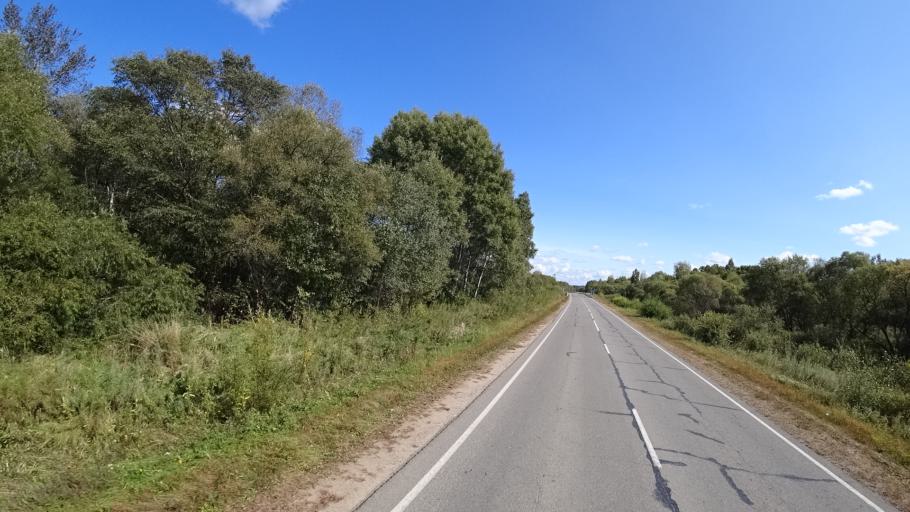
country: RU
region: Amur
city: Arkhara
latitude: 49.4068
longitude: 130.1215
